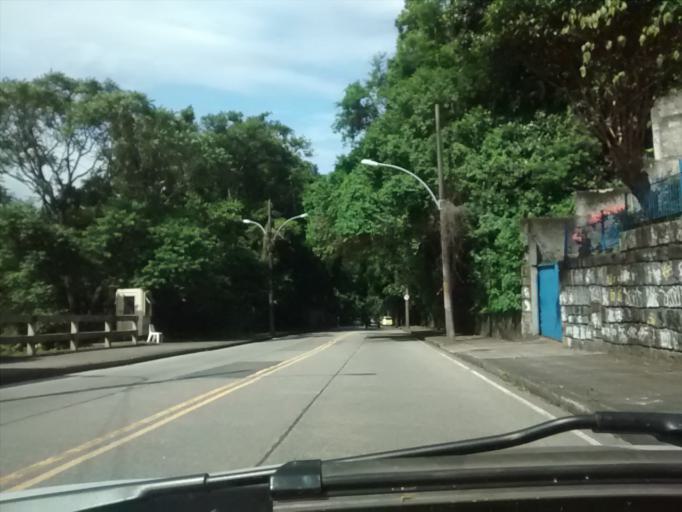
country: BR
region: Rio de Janeiro
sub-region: Rio De Janeiro
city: Rio de Janeiro
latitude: -22.9535
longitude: -43.2619
